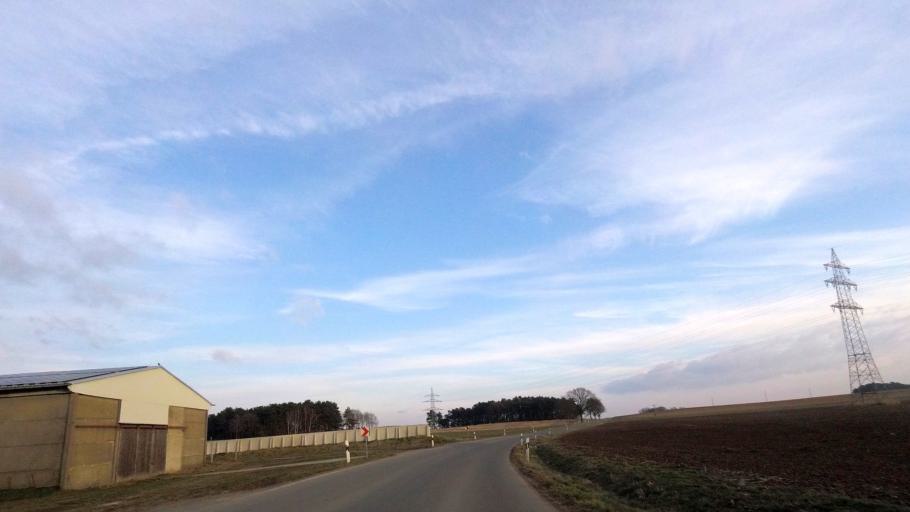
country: DE
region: Brandenburg
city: Belzig
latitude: 52.0963
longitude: 12.6227
